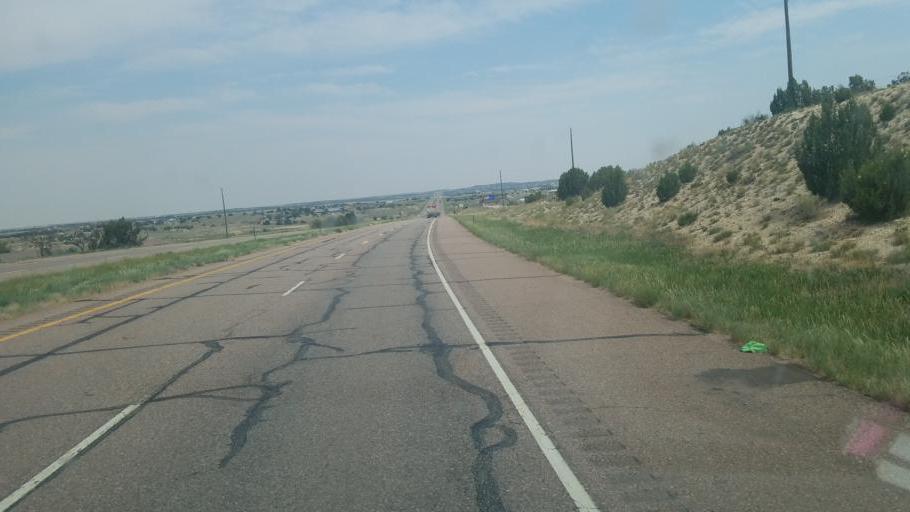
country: US
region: Colorado
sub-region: Fremont County
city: Penrose
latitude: 38.4027
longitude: -104.9838
